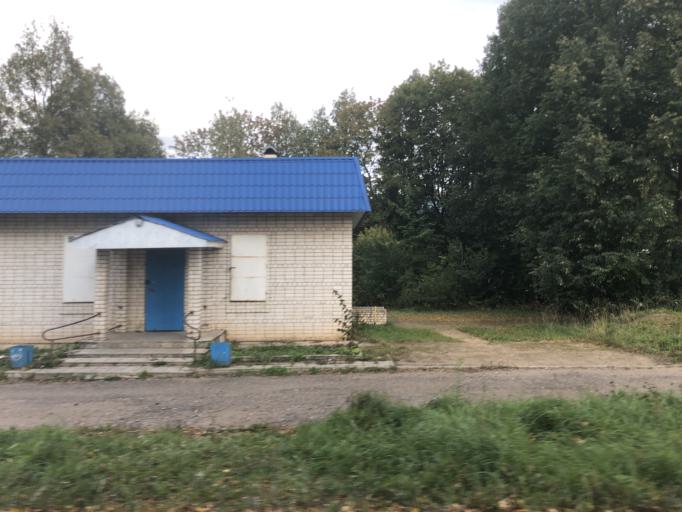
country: RU
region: Tverskaya
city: Rzhev
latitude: 56.2525
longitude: 34.2930
